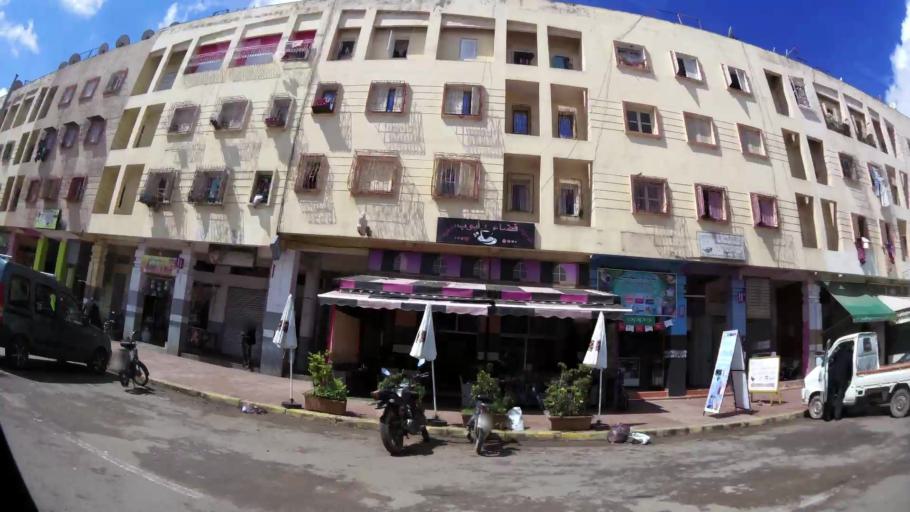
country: MA
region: Grand Casablanca
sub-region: Mediouna
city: Tit Mellil
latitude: 33.5510
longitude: -7.4839
